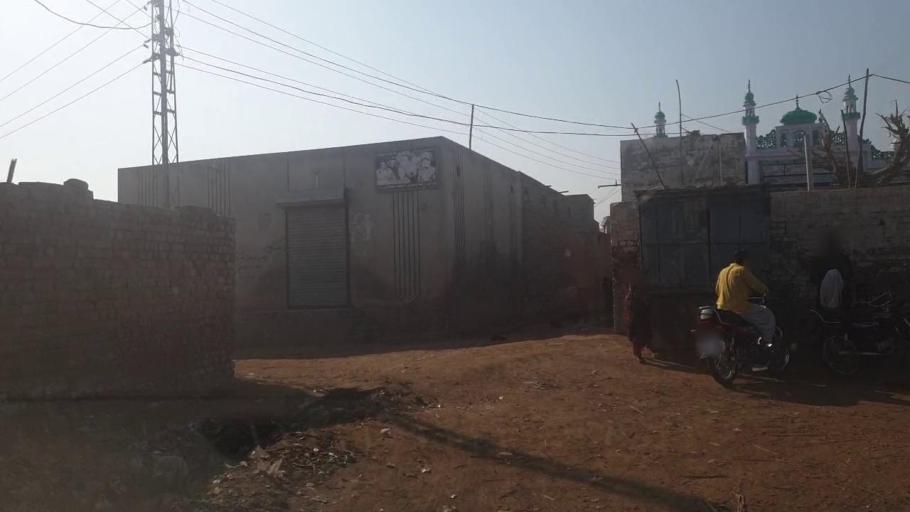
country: PK
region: Sindh
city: Sakrand
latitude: 26.0644
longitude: 68.3787
